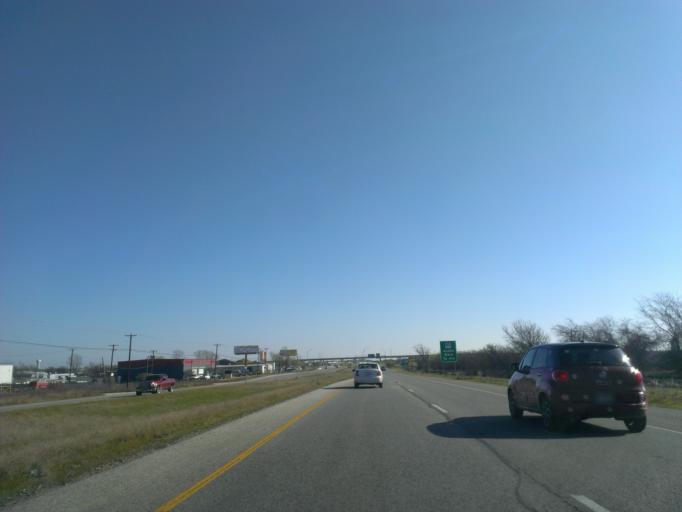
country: US
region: Texas
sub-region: Williamson County
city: Hutto
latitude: 30.5360
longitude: -97.5868
